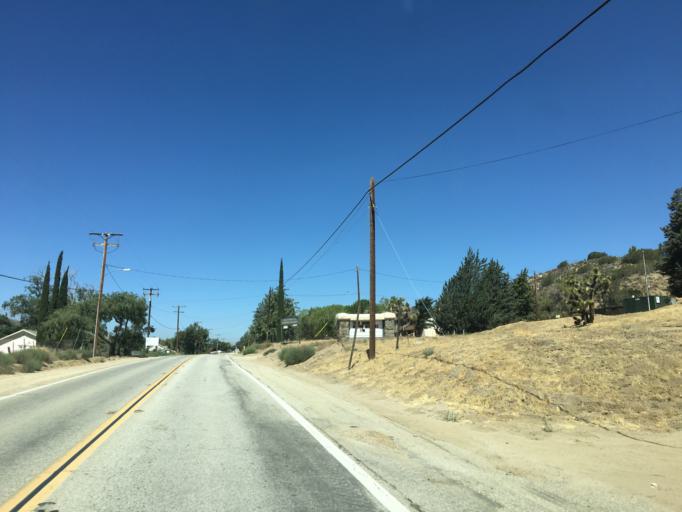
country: US
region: California
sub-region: Los Angeles County
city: Leona Valley
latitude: 34.6148
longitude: -118.2792
